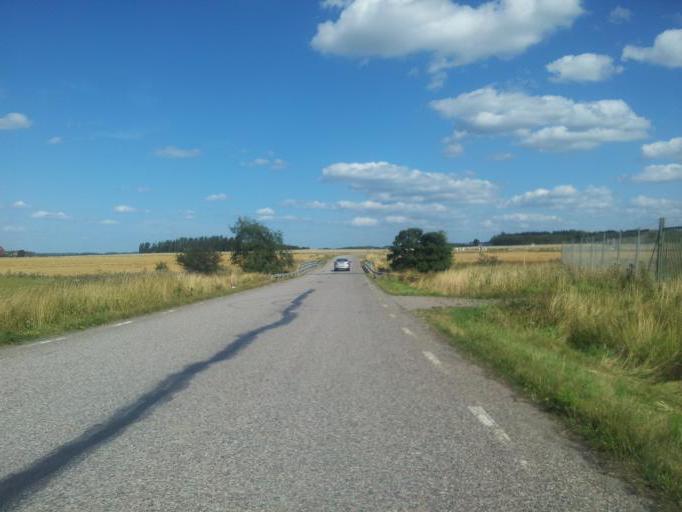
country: SE
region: Uppsala
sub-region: Uppsala Kommun
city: Gamla Uppsala
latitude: 59.9096
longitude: 17.6022
